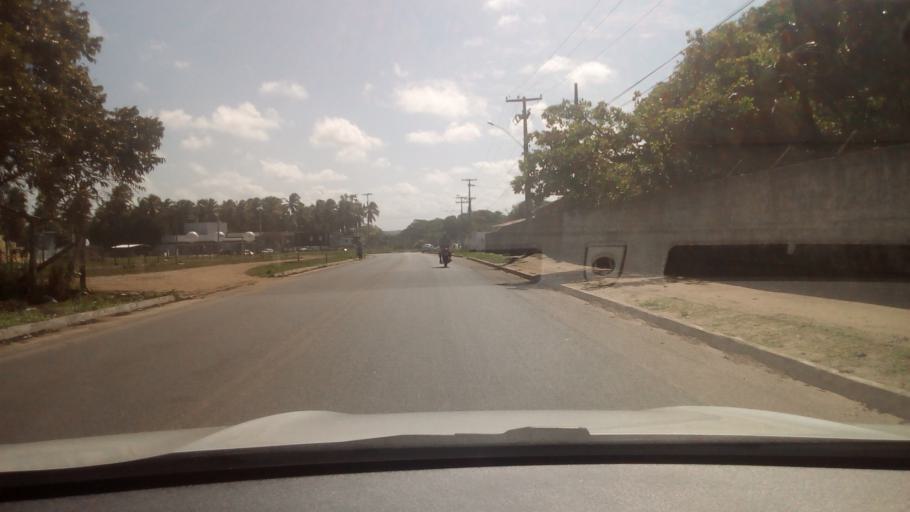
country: BR
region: Paraiba
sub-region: Conde
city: Conde
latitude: -7.2176
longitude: -34.8339
